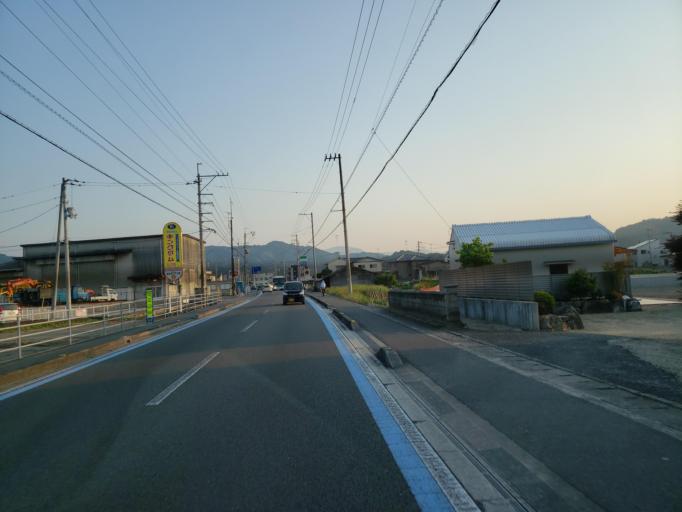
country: JP
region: Ehime
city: Hojo
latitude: 34.0399
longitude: 132.9746
